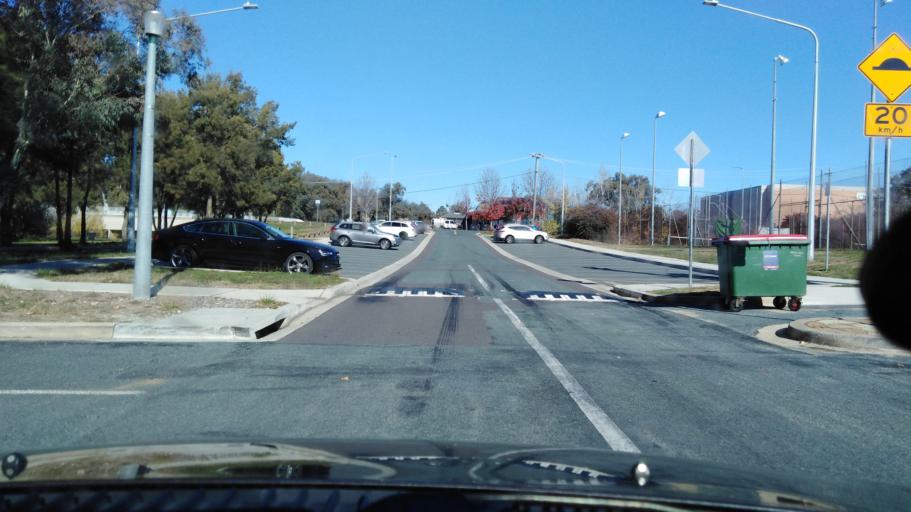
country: AU
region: Australian Capital Territory
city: Forrest
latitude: -35.3384
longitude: 149.0535
